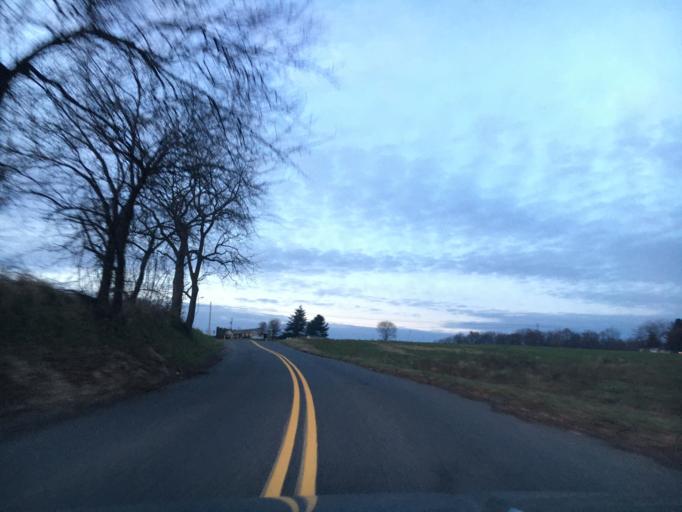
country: US
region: Pennsylvania
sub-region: Lehigh County
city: Schnecksville
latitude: 40.6872
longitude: -75.5729
